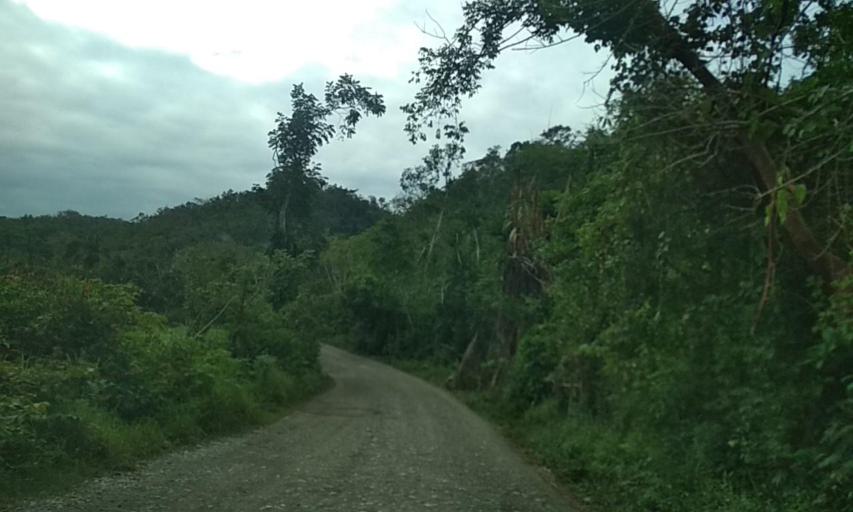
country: MX
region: Veracruz
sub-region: Papantla
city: Residencial Tajin
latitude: 20.6244
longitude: -97.3638
